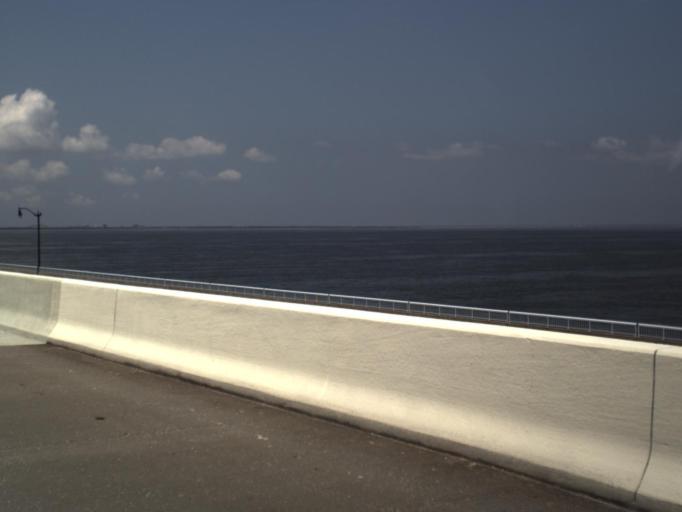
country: US
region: Florida
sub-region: Pinellas County
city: Gandy
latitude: 27.8849
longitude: -82.5627
